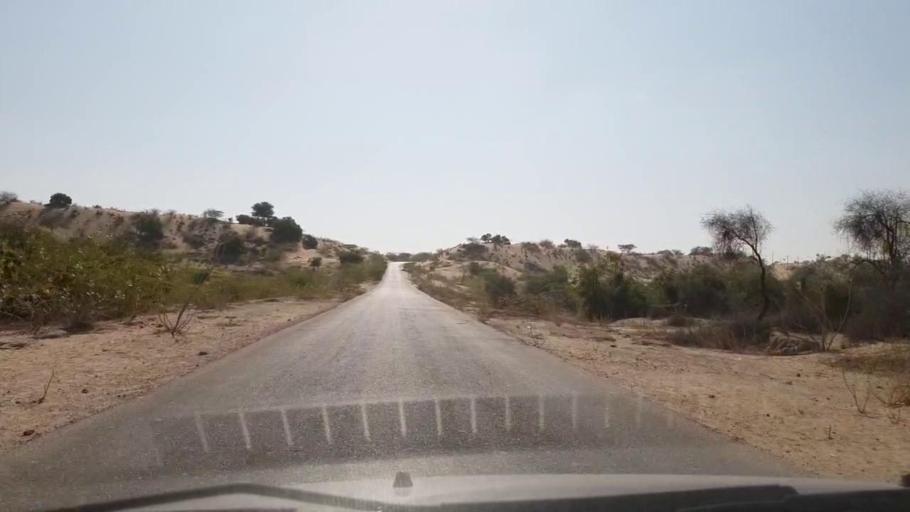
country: PK
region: Sindh
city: Mithi
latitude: 24.5932
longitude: 69.7128
